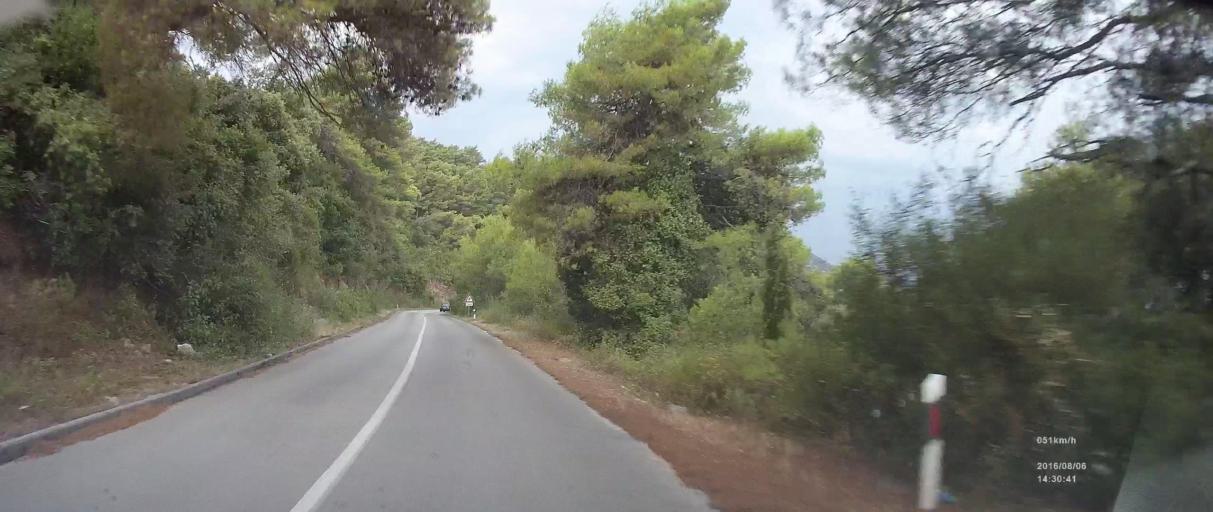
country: HR
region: Dubrovacko-Neretvanska
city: Ston
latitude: 42.7114
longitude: 17.7260
